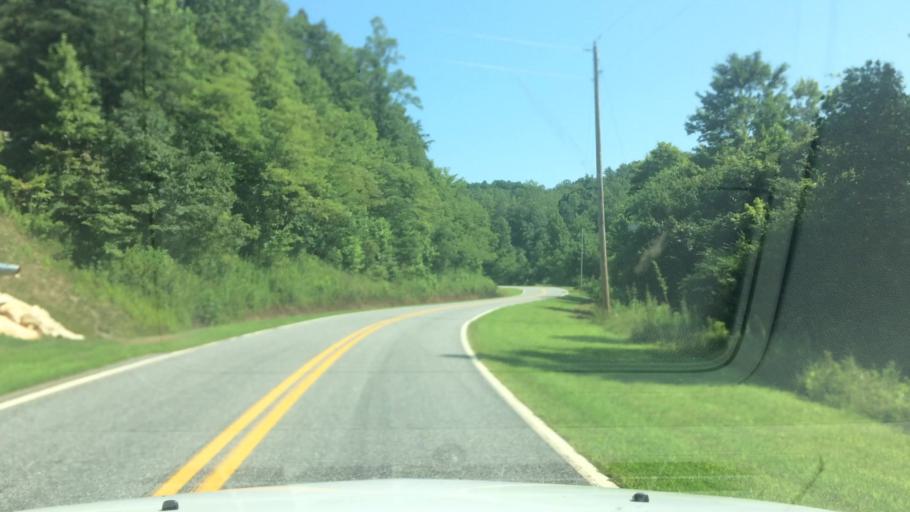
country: US
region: North Carolina
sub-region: Alexander County
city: Taylorsville
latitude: 35.9879
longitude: -81.2807
